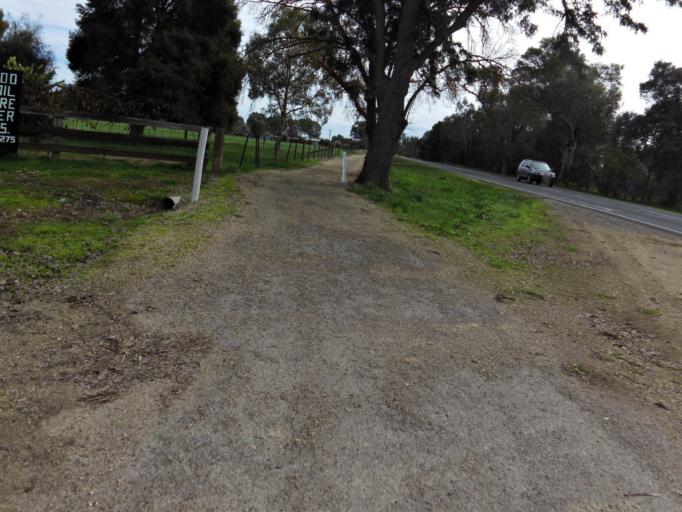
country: AU
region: Victoria
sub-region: Wangaratta
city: Wangaratta
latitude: -36.4084
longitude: 146.3505
